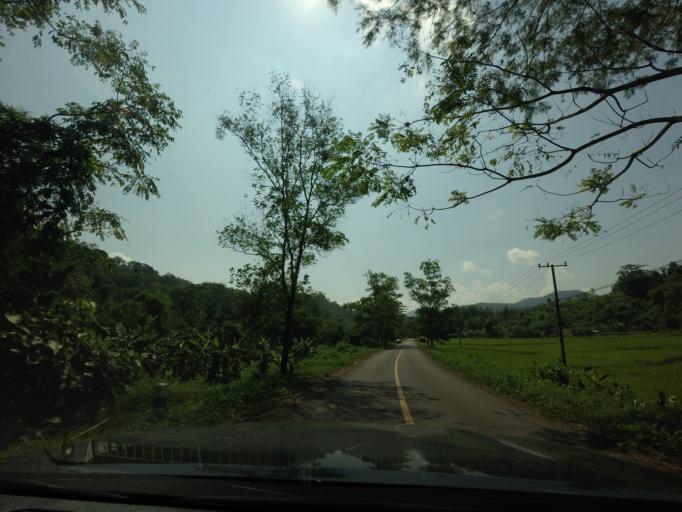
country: TH
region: Nan
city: Bo Kluea
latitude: 19.0406
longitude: 101.1712
